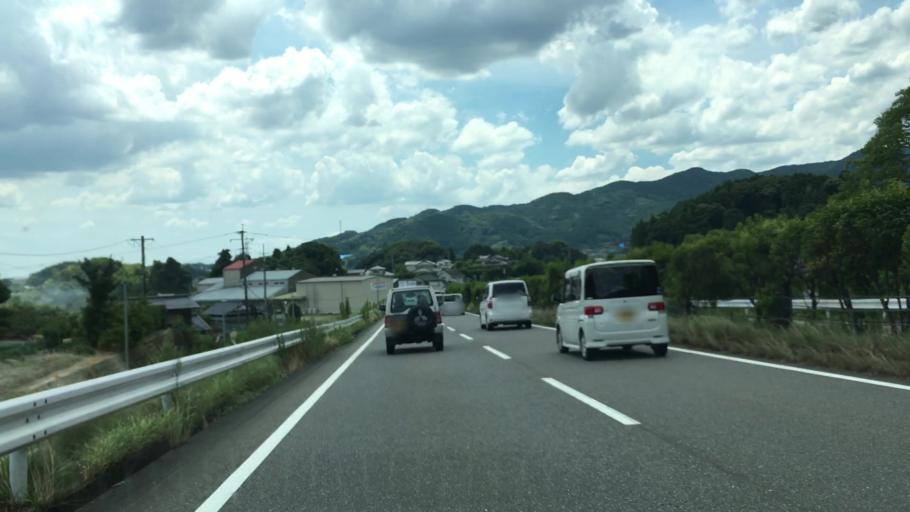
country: JP
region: Saga Prefecture
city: Tosu
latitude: 33.4277
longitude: 130.5181
